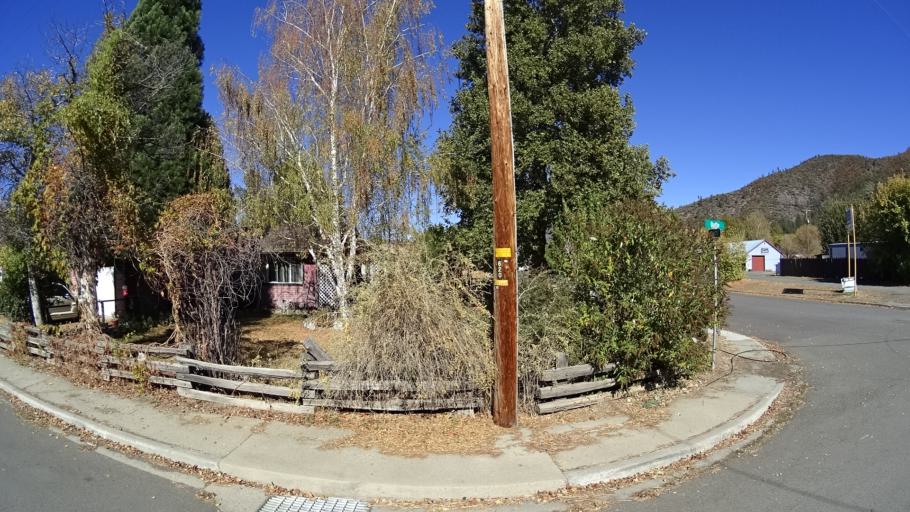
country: US
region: California
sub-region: Siskiyou County
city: Yreka
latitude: 41.6092
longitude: -122.8425
